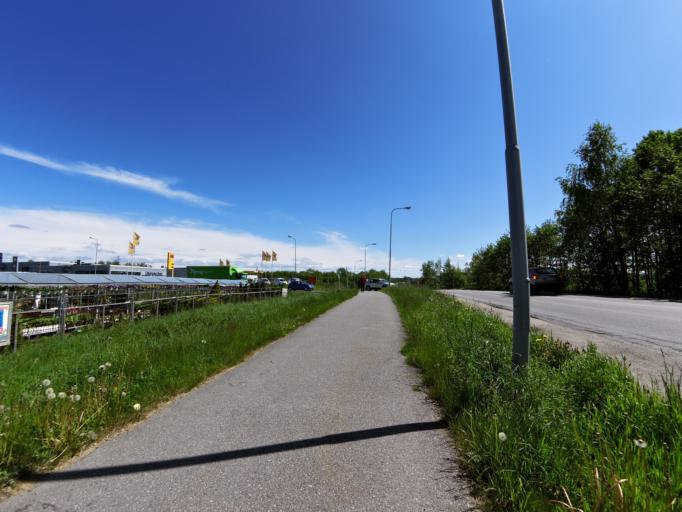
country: NO
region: Ostfold
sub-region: Fredrikstad
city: Fredrikstad
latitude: 59.2427
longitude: 10.9808
